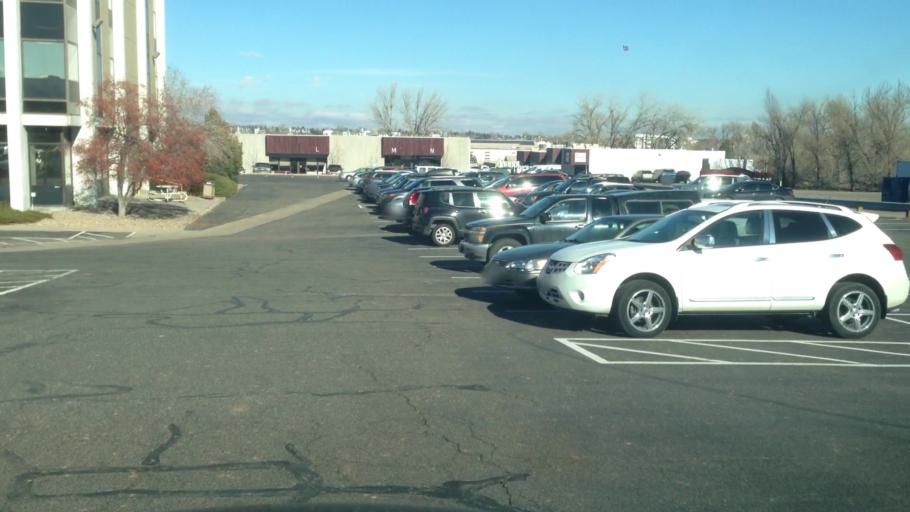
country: US
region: Colorado
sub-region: Jefferson County
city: Lakewood
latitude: 39.7293
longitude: -105.1225
